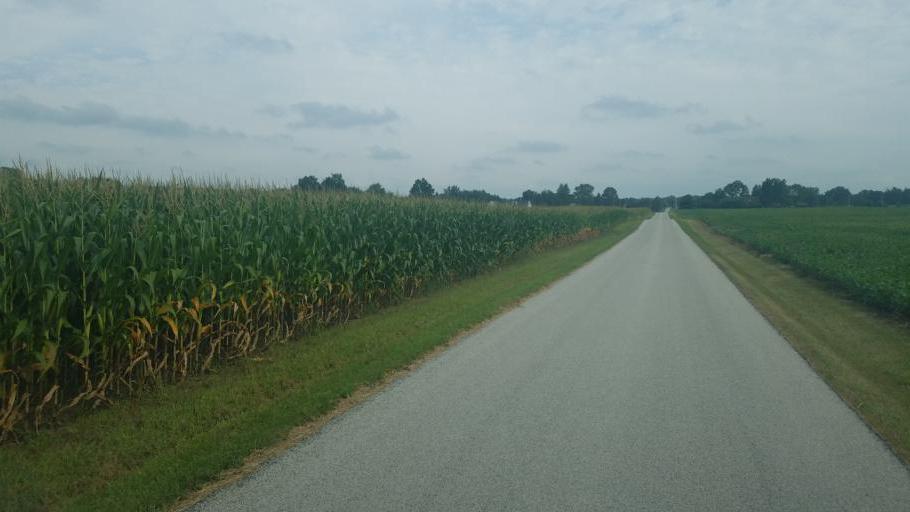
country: US
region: Ohio
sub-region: Morrow County
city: Cardington
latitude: 40.4986
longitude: -82.9391
